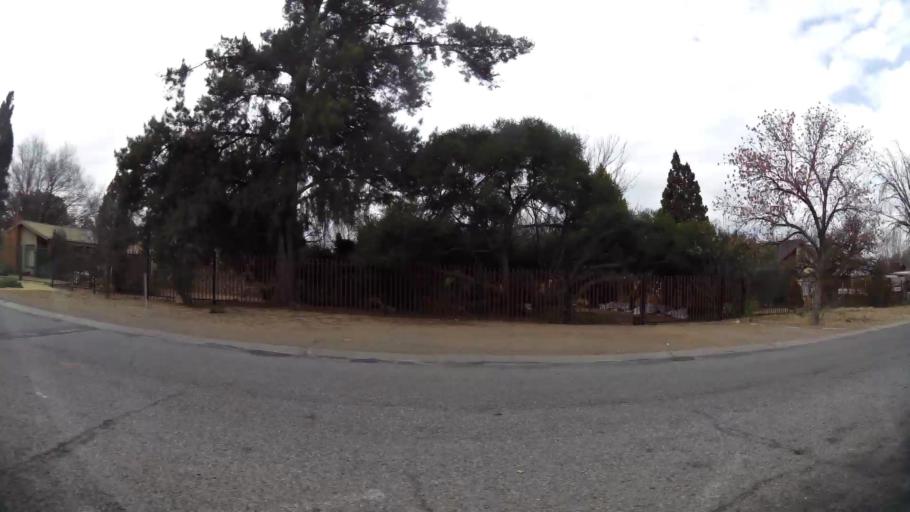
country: ZA
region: Orange Free State
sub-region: Fezile Dabi District Municipality
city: Kroonstad
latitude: -27.6472
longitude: 27.2387
